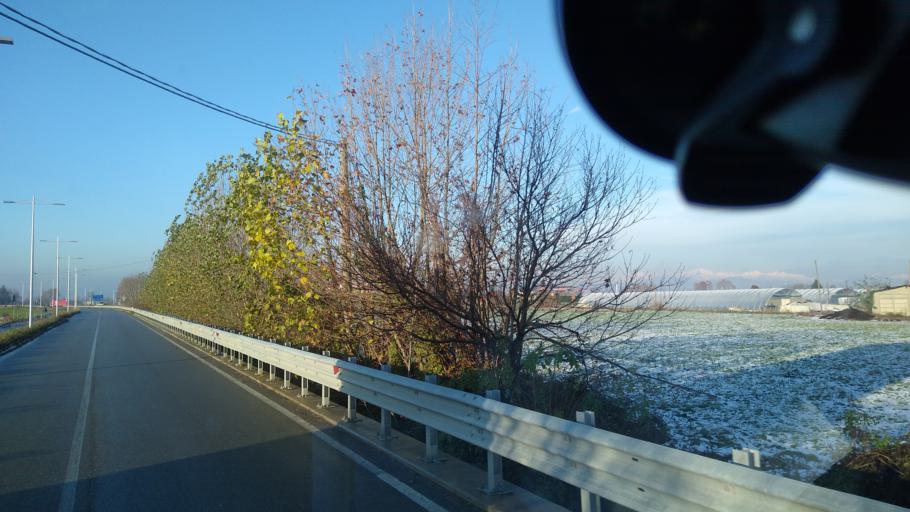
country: IT
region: Lombardy
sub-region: Provincia di Bergamo
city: Misano di Gera d'Adda
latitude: 45.4742
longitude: 9.6181
